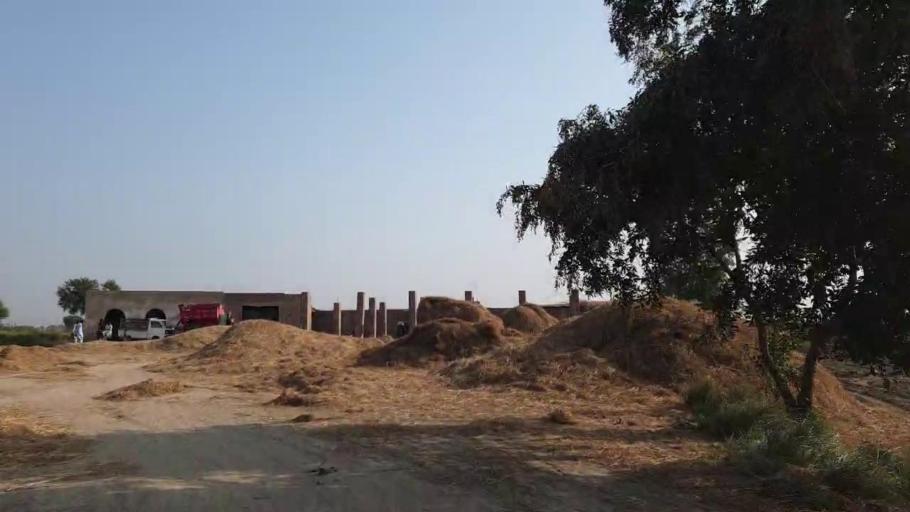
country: PK
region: Sindh
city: Bulri
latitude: 24.9714
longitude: 68.3772
